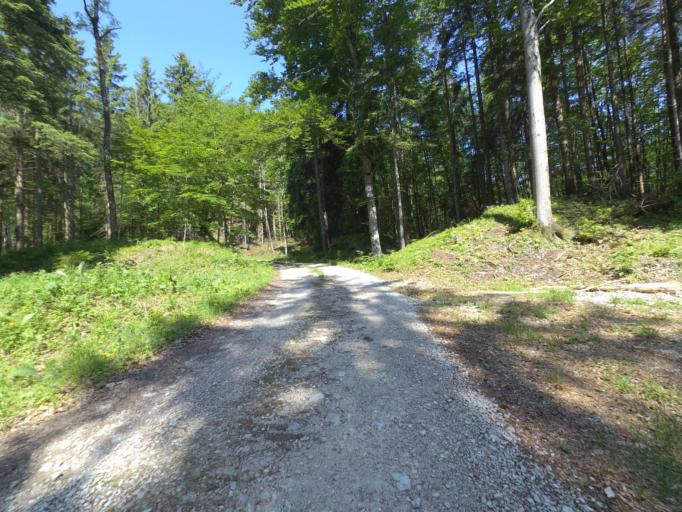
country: AT
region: Salzburg
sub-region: Politischer Bezirk Salzburg-Umgebung
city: Ebenau
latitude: 47.7851
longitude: 13.1528
